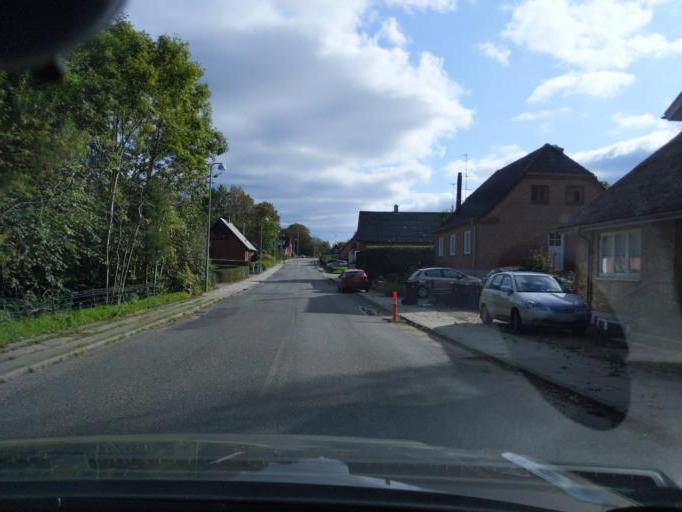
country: DK
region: North Denmark
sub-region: Mariagerfjord Kommune
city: Hobro
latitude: 56.5294
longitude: 9.7264
